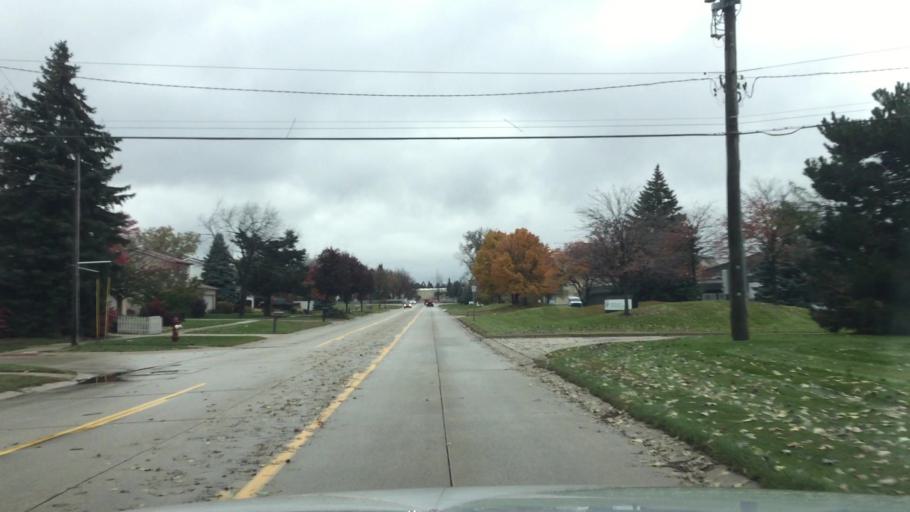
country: US
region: Michigan
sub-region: Macomb County
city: Utica
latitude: 42.6217
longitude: -83.0469
